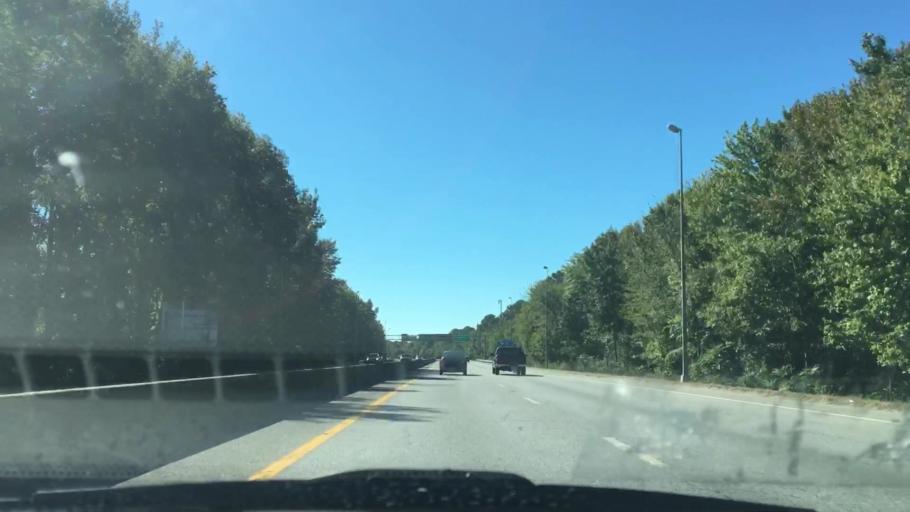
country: US
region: Virginia
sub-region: City of Portsmouth
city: Portsmouth Heights
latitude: 36.8056
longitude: -76.3636
